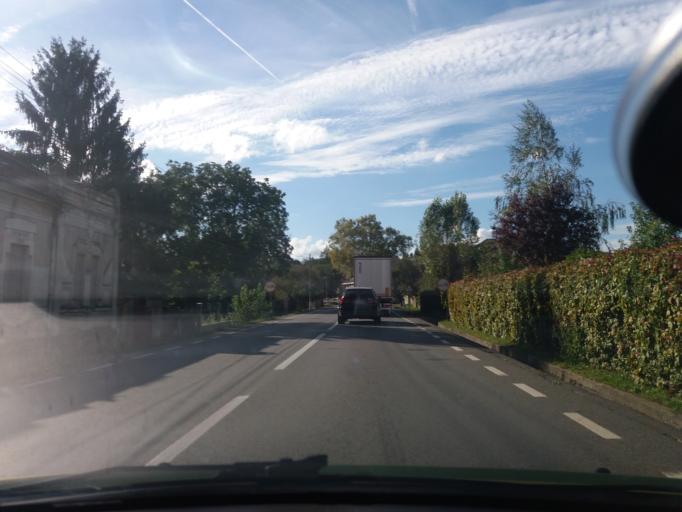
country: RO
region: Arad
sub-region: Comuna Barzava
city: Barzava
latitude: 46.1057
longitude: 21.9963
